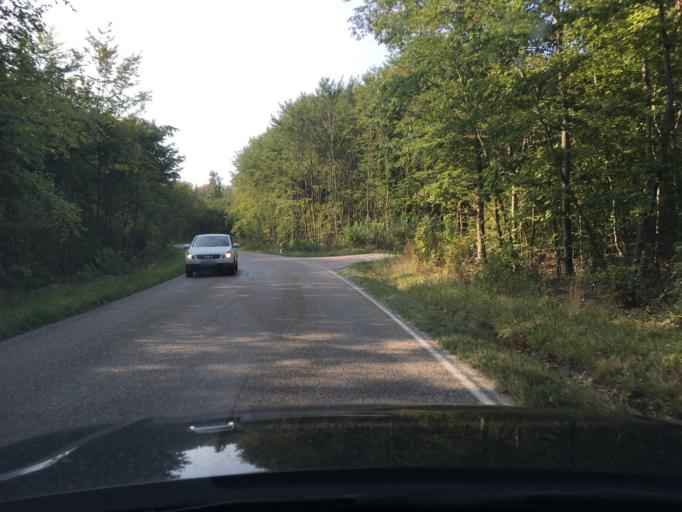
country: DE
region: Baden-Wuerttemberg
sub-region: Regierungsbezirk Stuttgart
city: Pfaffenhofen
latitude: 49.0858
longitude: 8.9520
